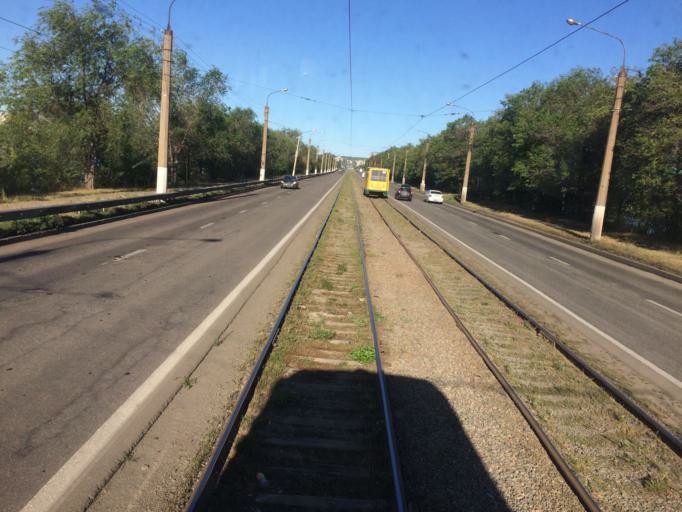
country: RU
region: Chelyabinsk
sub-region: Gorod Magnitogorsk
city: Magnitogorsk
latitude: 53.3981
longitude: 59.0097
